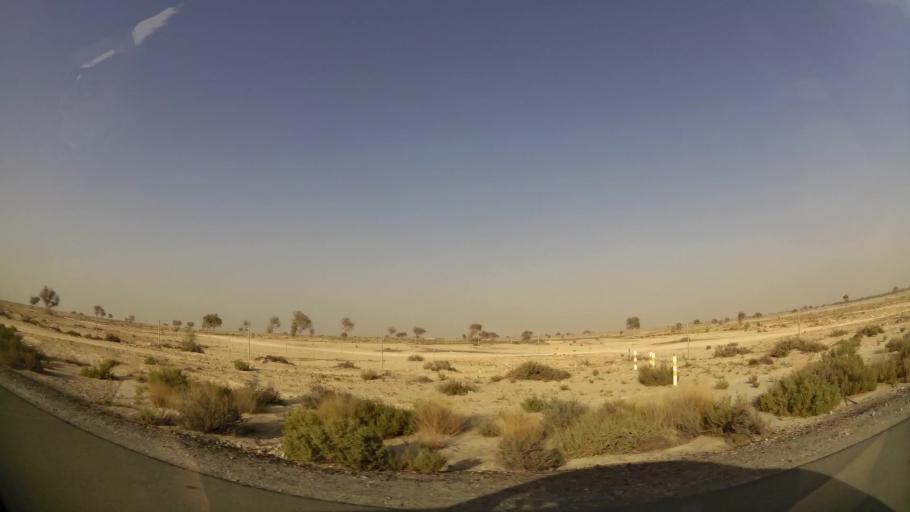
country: AE
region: Dubai
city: Dubai
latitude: 25.0711
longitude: 55.2501
